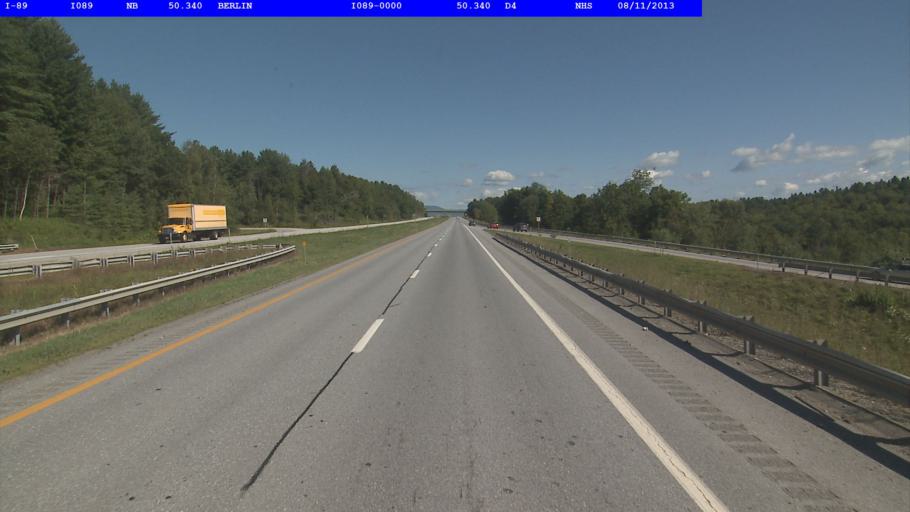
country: US
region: Vermont
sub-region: Washington County
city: Montpelier
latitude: 44.2162
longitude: -72.5837
